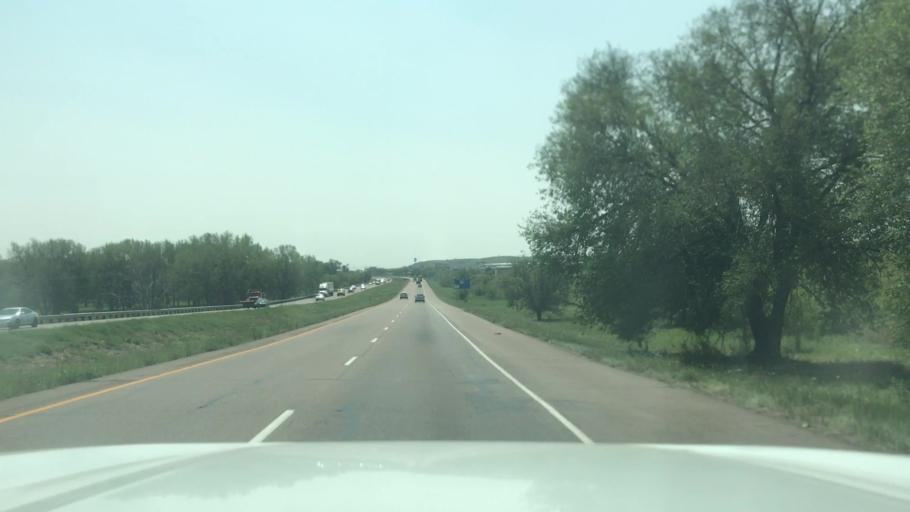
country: US
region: Colorado
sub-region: El Paso County
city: Fountain
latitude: 38.6855
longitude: -104.7167
